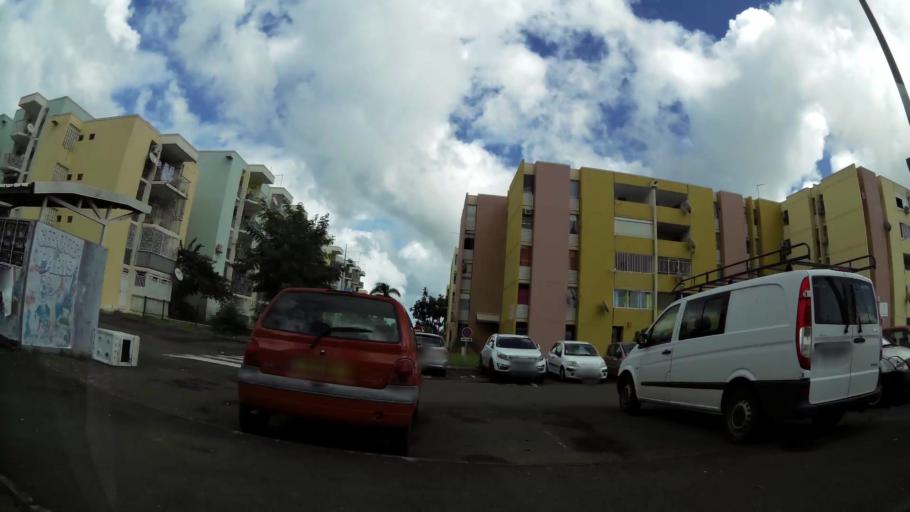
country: GP
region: Guadeloupe
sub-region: Guadeloupe
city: Pointe-a-Pitre
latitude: 16.2504
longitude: -61.5460
